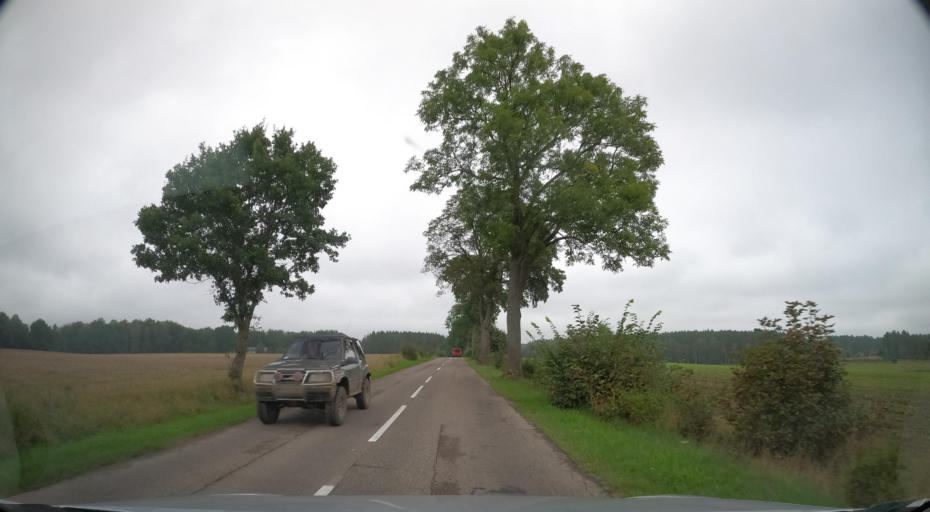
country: PL
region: Pomeranian Voivodeship
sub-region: Powiat wejherowski
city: Luzino
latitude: 54.4866
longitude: 18.1132
